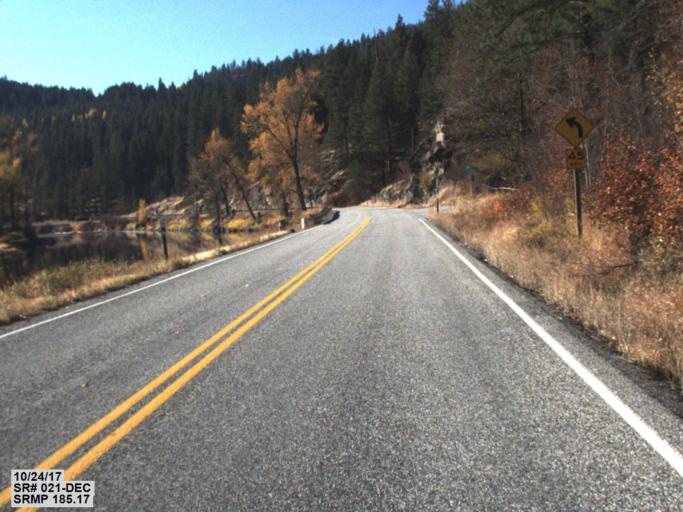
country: CA
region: British Columbia
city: Grand Forks
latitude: 48.9303
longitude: -118.5637
